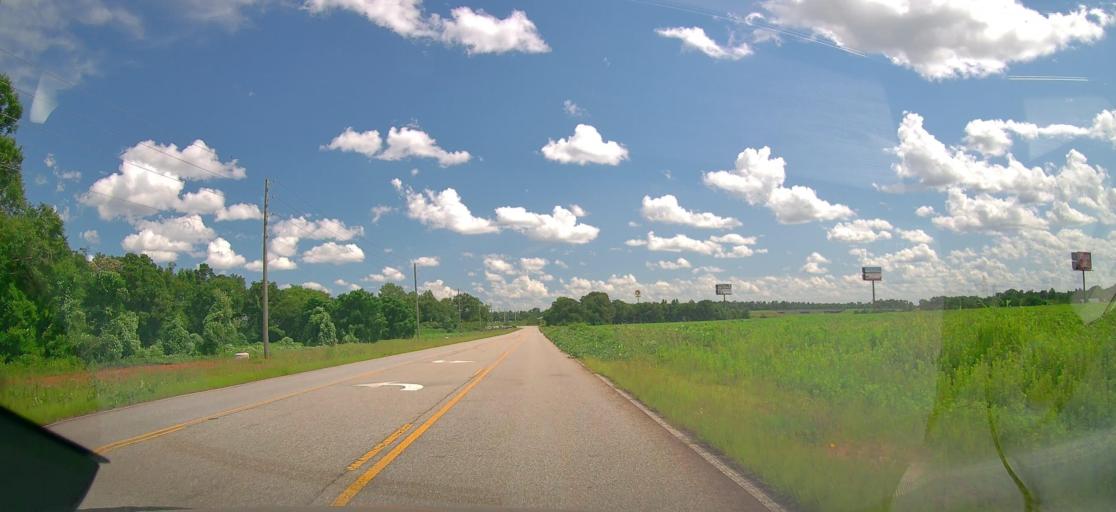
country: US
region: Georgia
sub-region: Houston County
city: Centerville
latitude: 32.5934
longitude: -83.7392
